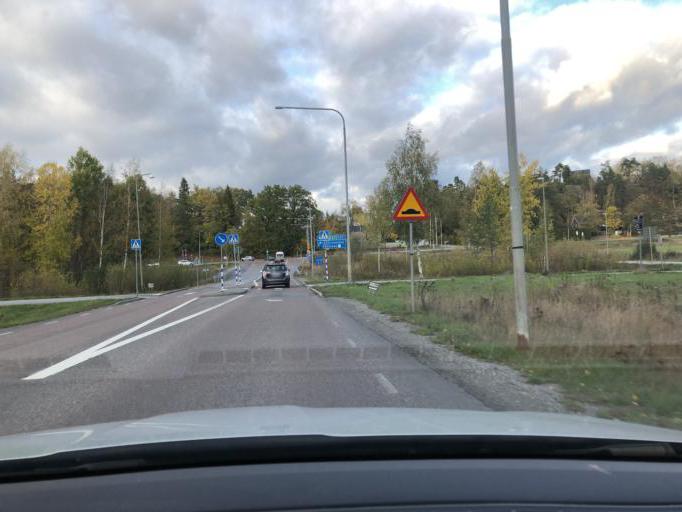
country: SE
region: Stockholm
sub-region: Huddinge Kommun
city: Huddinge
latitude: 59.2293
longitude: 17.9374
